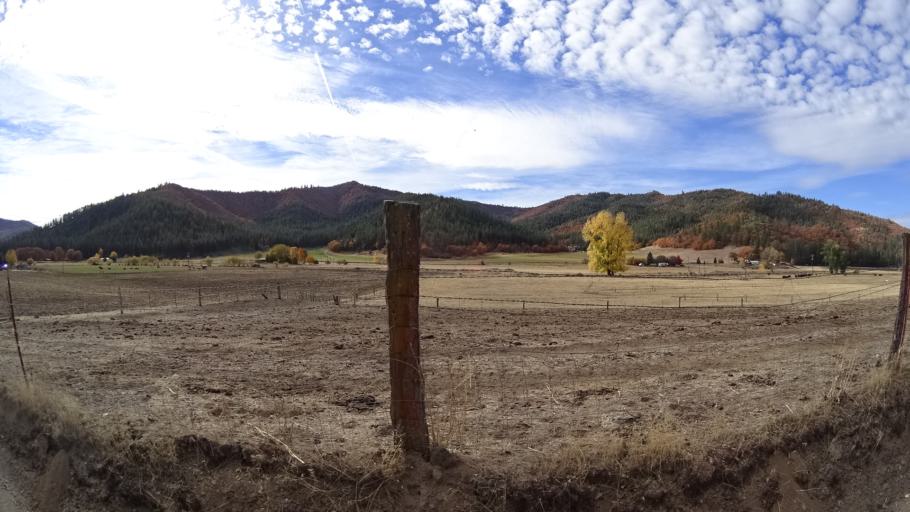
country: US
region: California
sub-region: Siskiyou County
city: Yreka
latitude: 41.6268
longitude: -122.8036
